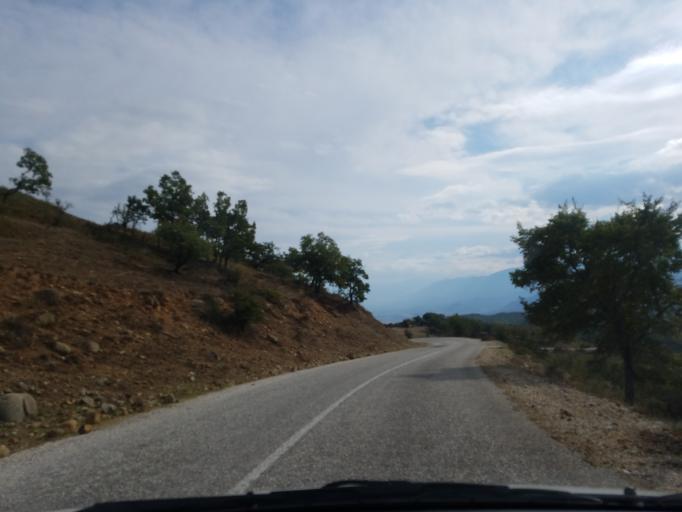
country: GR
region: Thessaly
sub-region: Trikala
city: Kastraki
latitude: 39.7512
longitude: 21.6615
